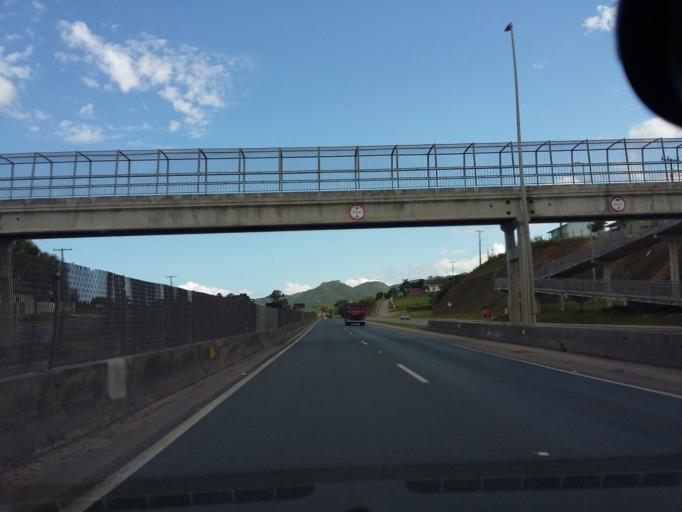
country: BR
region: Santa Catarina
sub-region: Biguacu
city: Biguacu
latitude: -27.3836
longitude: -48.6313
